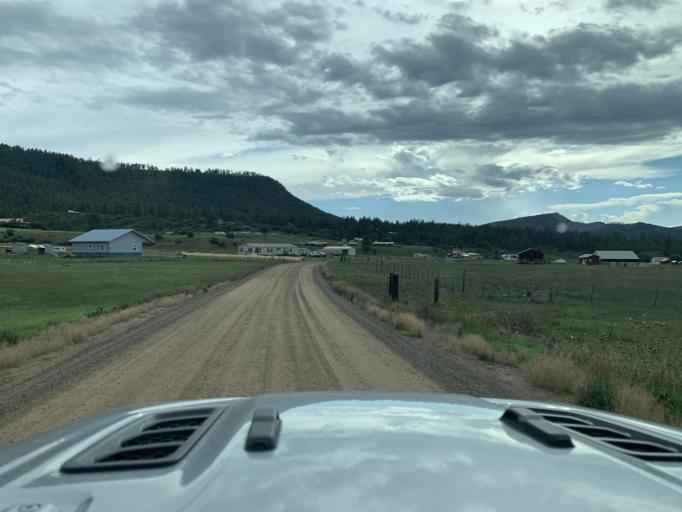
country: US
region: Colorado
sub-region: Archuleta County
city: Pagosa Springs
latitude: 37.2211
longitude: -107.1852
